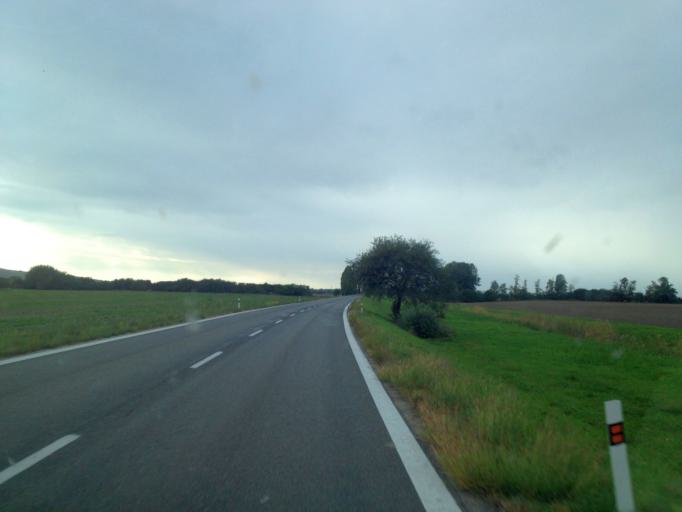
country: HU
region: Komarom-Esztergom
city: Labatlan
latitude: 47.7612
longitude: 18.5164
